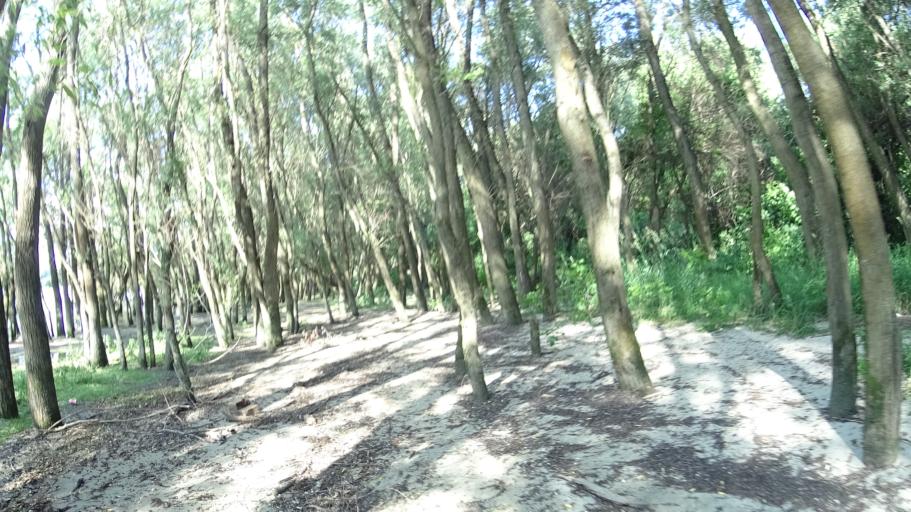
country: HU
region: Pest
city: Visegrad
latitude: 47.8098
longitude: 18.9900
